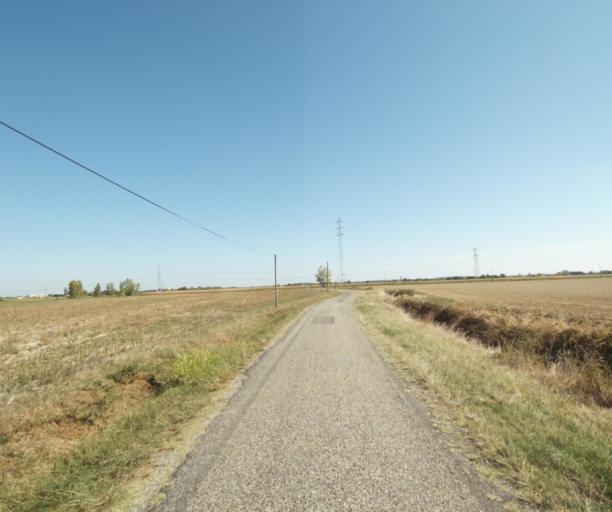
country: FR
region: Midi-Pyrenees
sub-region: Departement du Tarn-et-Garonne
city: Verdun-sur-Garonne
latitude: 43.8353
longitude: 1.2146
